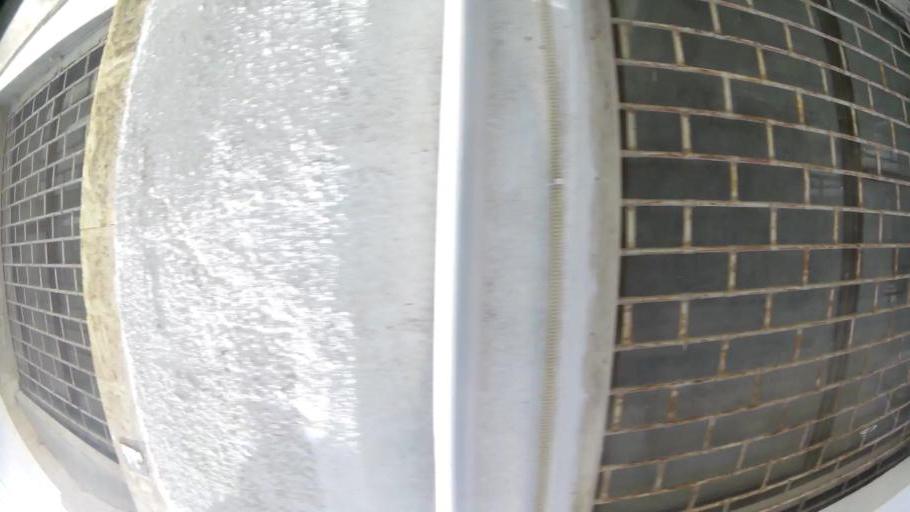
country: CY
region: Lefkosia
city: Nicosia
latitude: 35.1781
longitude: 33.3627
